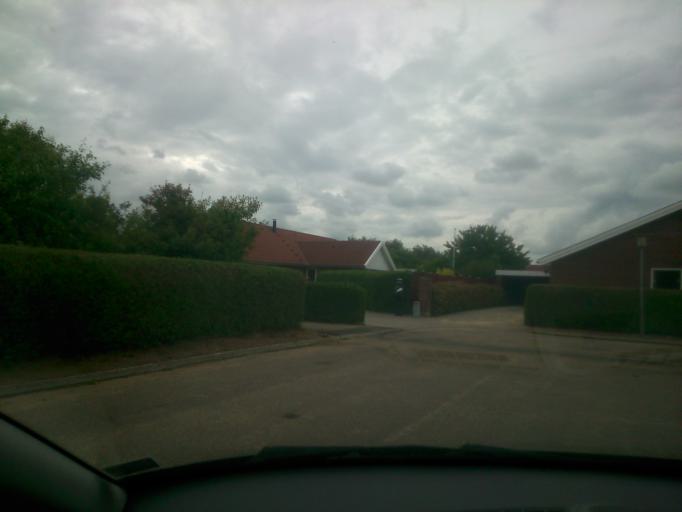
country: DK
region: South Denmark
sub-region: Esbjerg Kommune
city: Esbjerg
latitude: 55.5206
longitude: 8.4231
